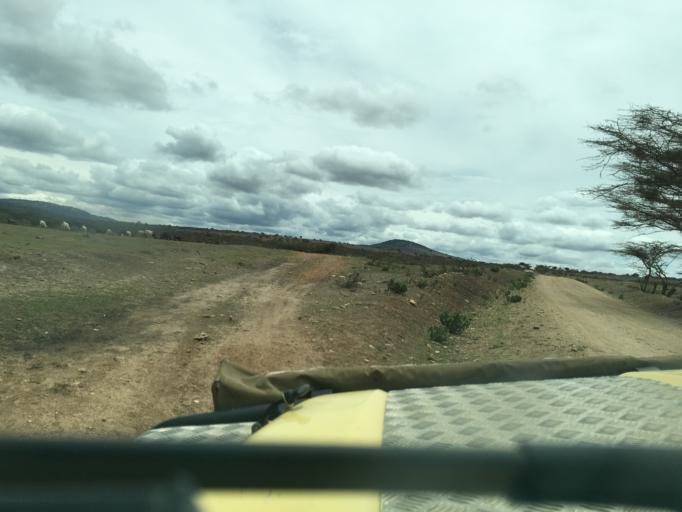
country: KE
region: Kajiado
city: Magadi
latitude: -2.1355
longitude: 35.5683
